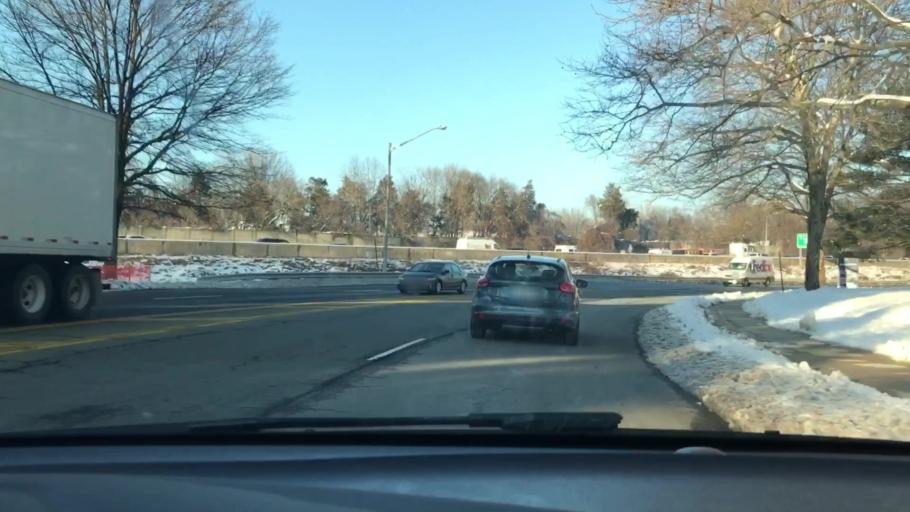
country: US
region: Virginia
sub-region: Fairfax County
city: Merrifield
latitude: 38.8799
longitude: -77.2360
